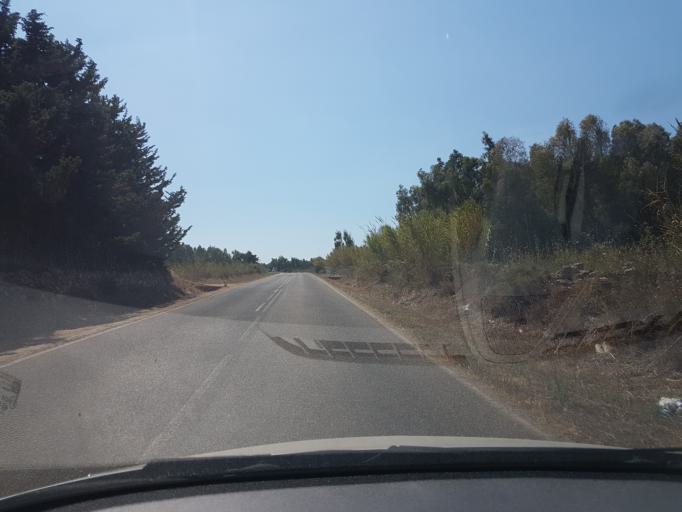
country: IT
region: Sardinia
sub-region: Provincia di Oristano
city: Riola Sardo
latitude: 39.9959
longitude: 8.4771
